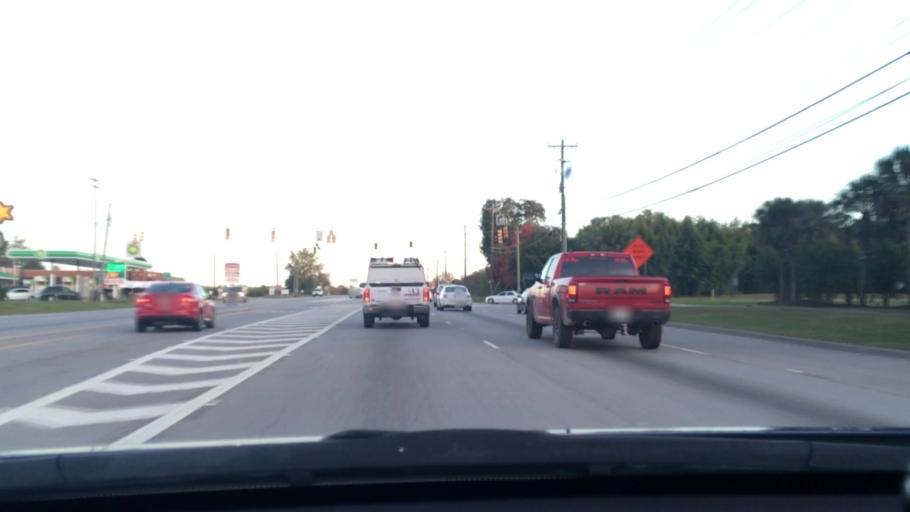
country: US
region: South Carolina
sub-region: Richland County
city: Hopkins
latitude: 33.9534
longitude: -80.9225
